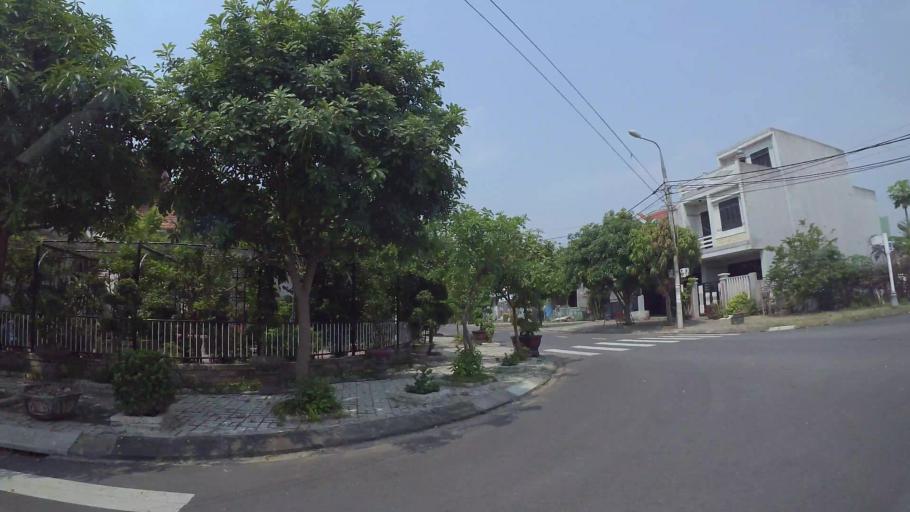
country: VN
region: Da Nang
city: Cam Le
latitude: 15.9868
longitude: 108.2161
